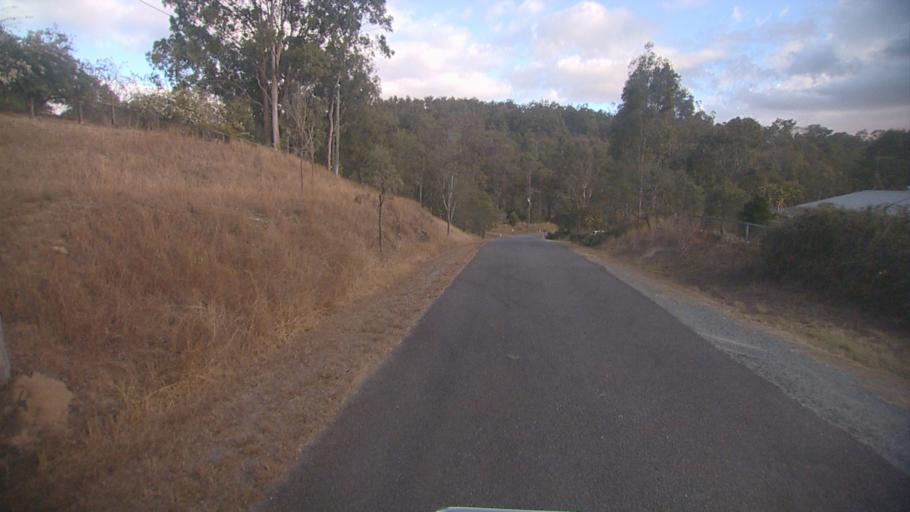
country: AU
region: Queensland
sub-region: Logan
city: Cedar Vale
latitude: -27.9039
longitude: 153.0733
